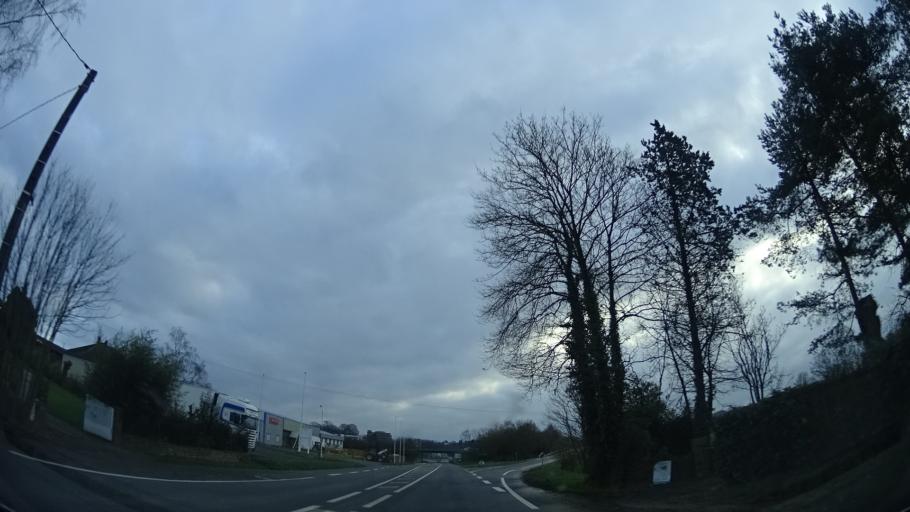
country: FR
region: Brittany
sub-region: Departement d'Ille-et-Vilaine
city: Poce-les-Bois
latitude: 48.1231
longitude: -1.2360
